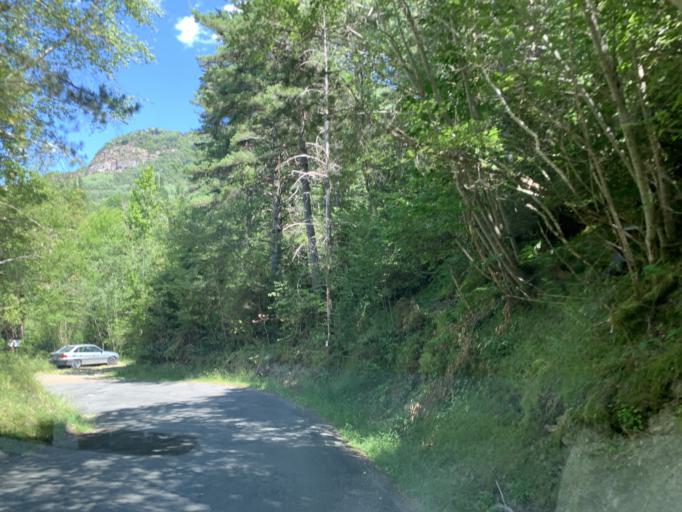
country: ES
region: Aragon
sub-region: Provincia de Huesca
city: Hoz de Jaca
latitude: 42.6985
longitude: -0.3048
